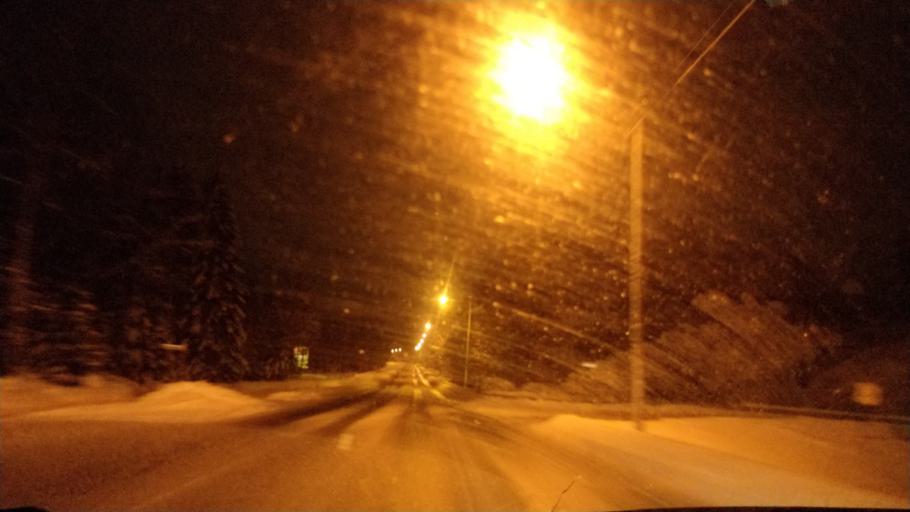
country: FI
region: Lapland
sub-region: Rovaniemi
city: Rovaniemi
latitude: 66.3840
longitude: 25.3774
